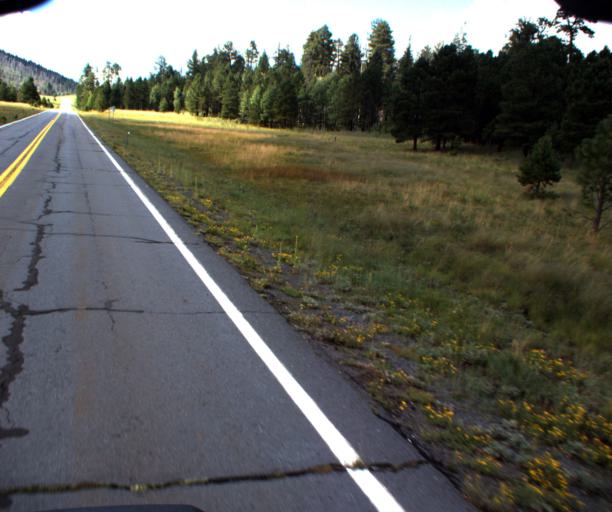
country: US
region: Arizona
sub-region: Apache County
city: Eagar
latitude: 33.9241
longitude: -109.4122
